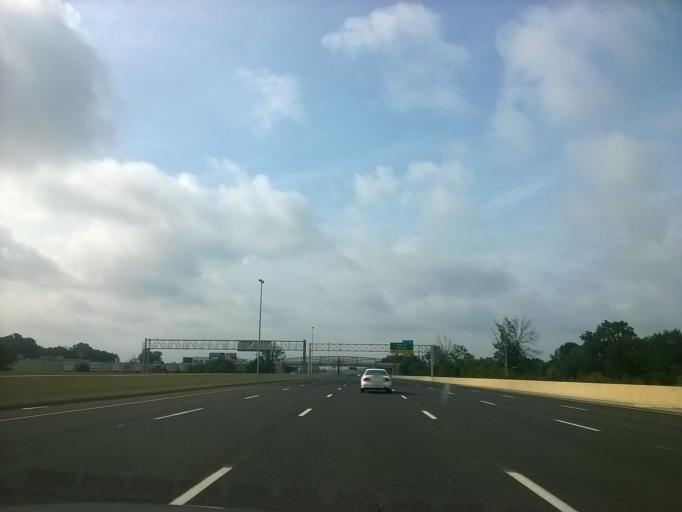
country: US
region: Indiana
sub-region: Boone County
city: Zionsville
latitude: 39.8994
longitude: -86.2699
